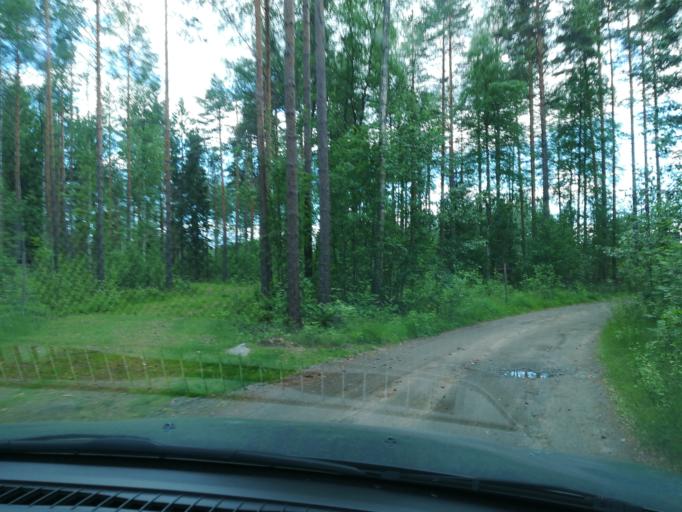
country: FI
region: Southern Savonia
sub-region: Mikkeli
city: Hirvensalmi
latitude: 61.6503
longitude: 26.7779
